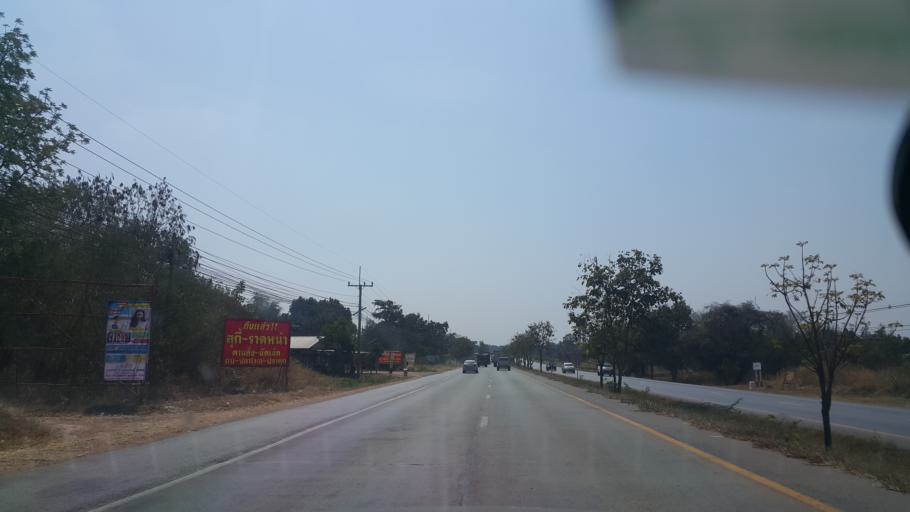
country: TH
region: Khon Kaen
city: Phon
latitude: 15.8456
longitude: 102.6157
